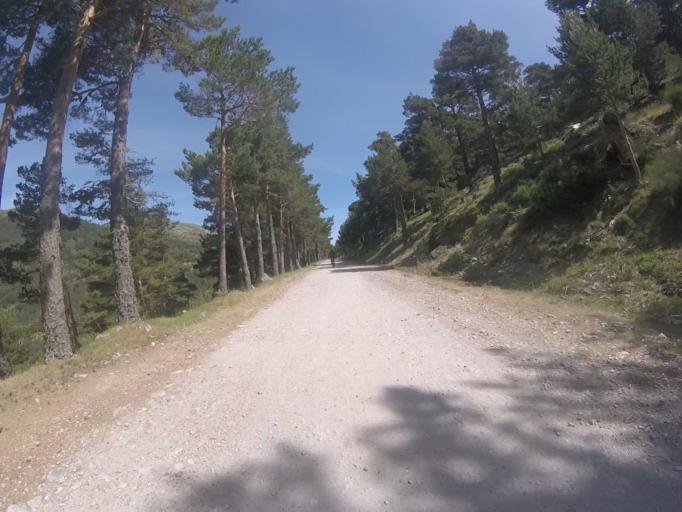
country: ES
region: Madrid
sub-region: Provincia de Madrid
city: Cercedilla
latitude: 40.7881
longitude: -4.0591
